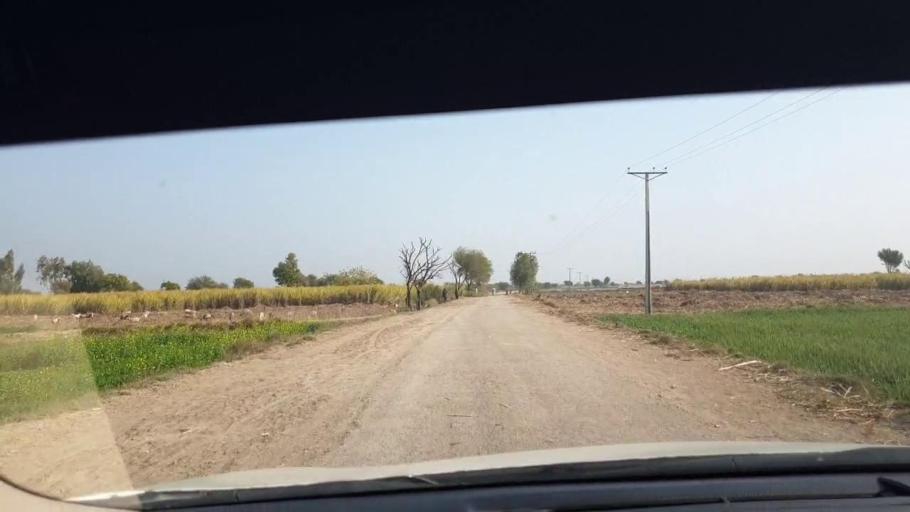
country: PK
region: Sindh
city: Berani
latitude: 25.8206
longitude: 68.7713
